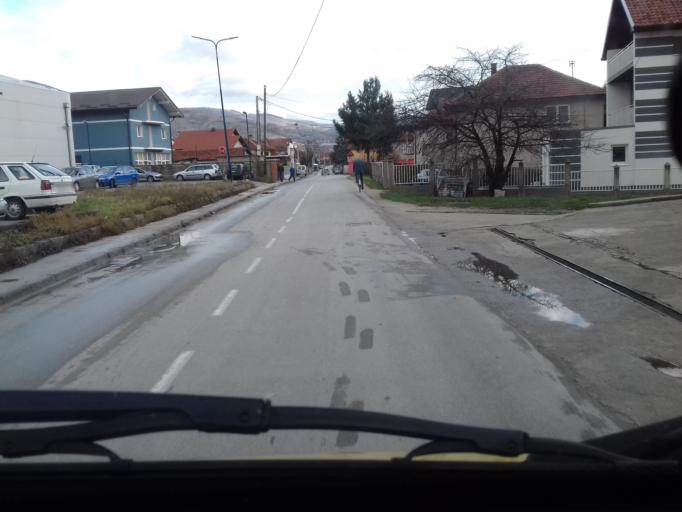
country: BA
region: Federation of Bosnia and Herzegovina
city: Zenica
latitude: 44.1916
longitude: 17.9375
